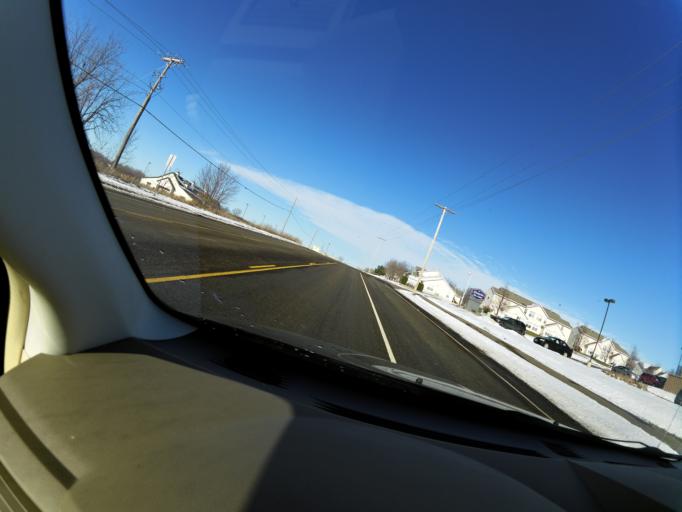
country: US
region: Minnesota
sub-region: Olmsted County
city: Rochester
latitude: 44.0842
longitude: -92.5088
